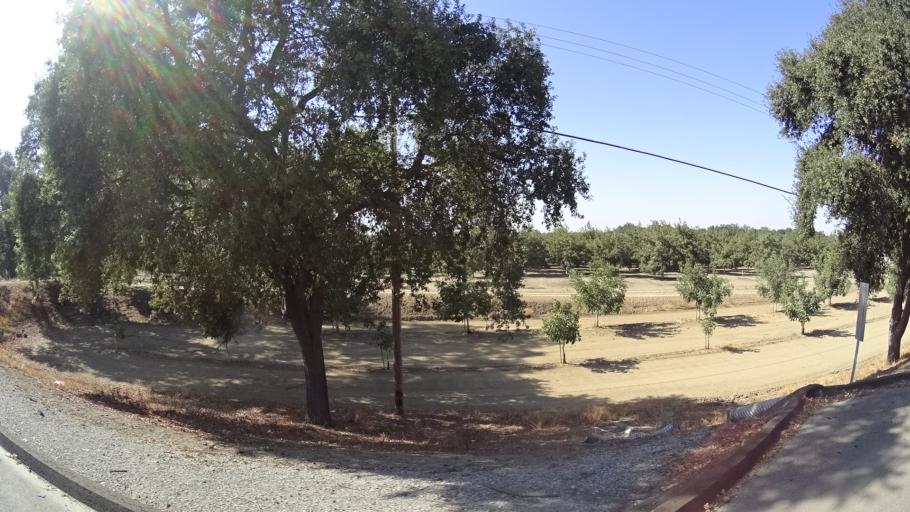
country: US
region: California
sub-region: Yolo County
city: West Sacramento
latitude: 38.6398
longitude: -121.5654
